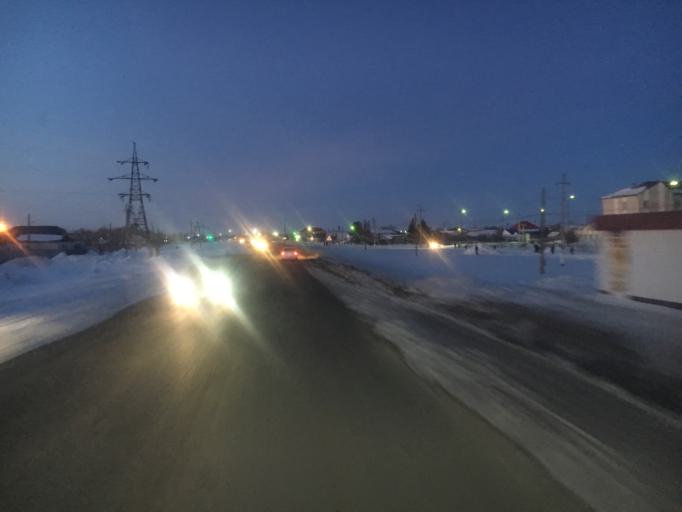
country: KZ
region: Batys Qazaqstan
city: Oral
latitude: 51.1468
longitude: 51.4882
